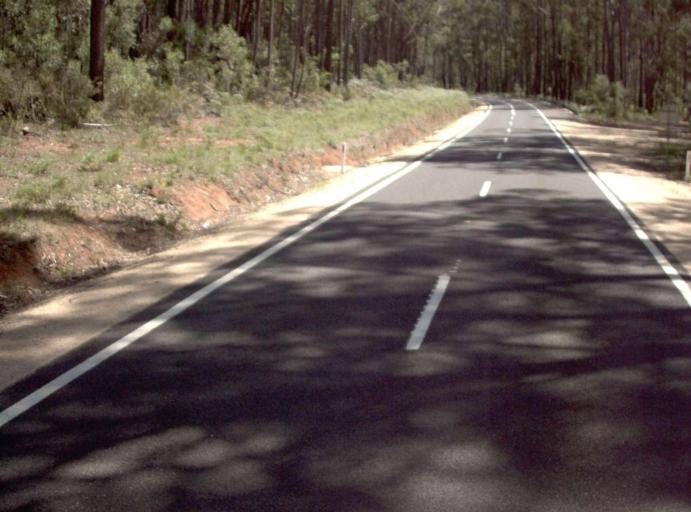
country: AU
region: New South Wales
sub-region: Bombala
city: Bombala
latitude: -37.5761
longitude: 149.0191
